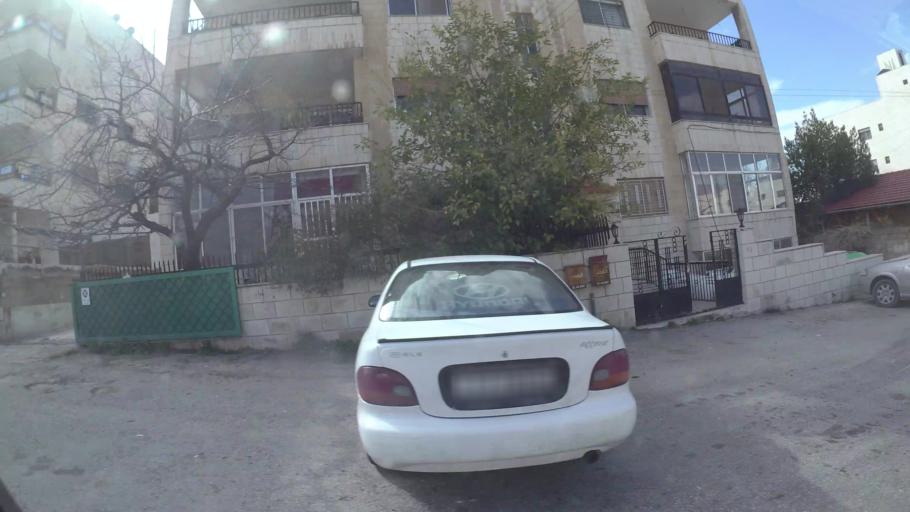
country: JO
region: Amman
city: Al Jubayhah
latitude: 32.0226
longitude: 35.8543
